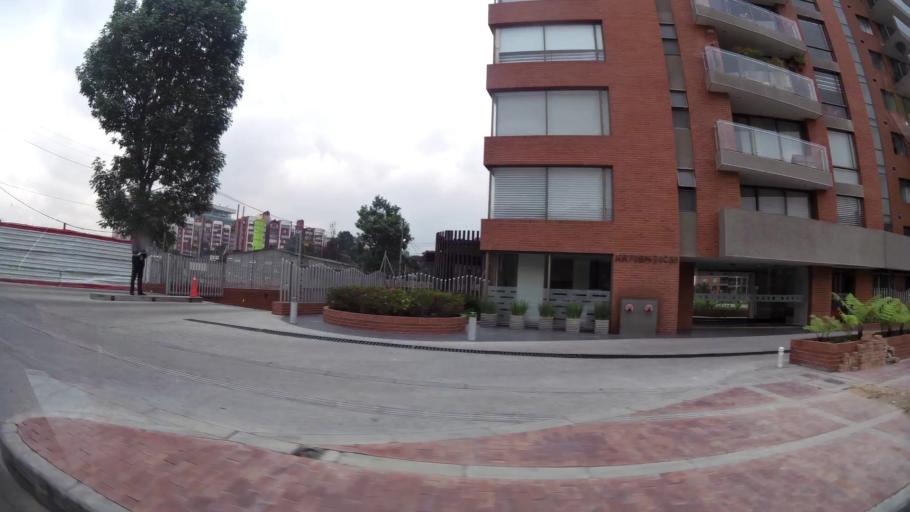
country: CO
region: Bogota D.C.
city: Bogota
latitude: 4.6617
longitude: -74.1128
